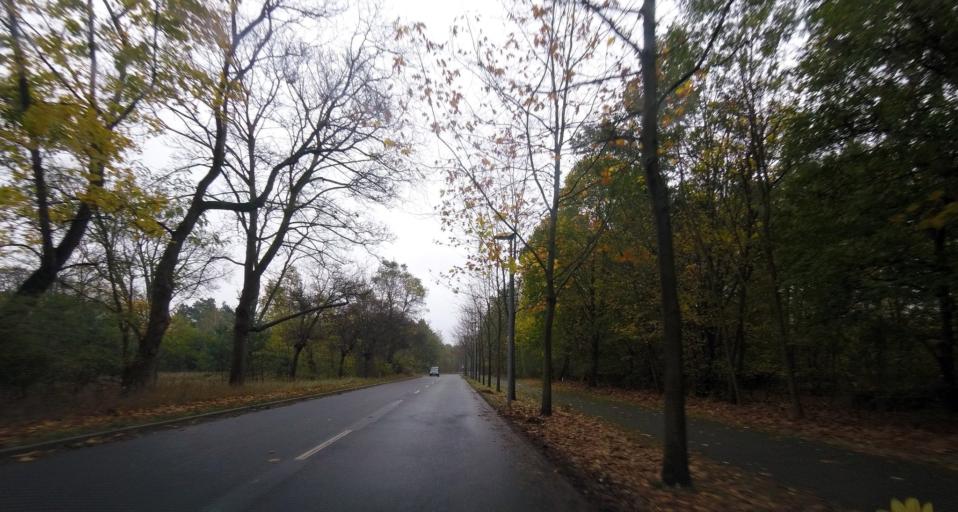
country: DE
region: Brandenburg
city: Niedergorsdorf
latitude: 52.0042
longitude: 12.9973
